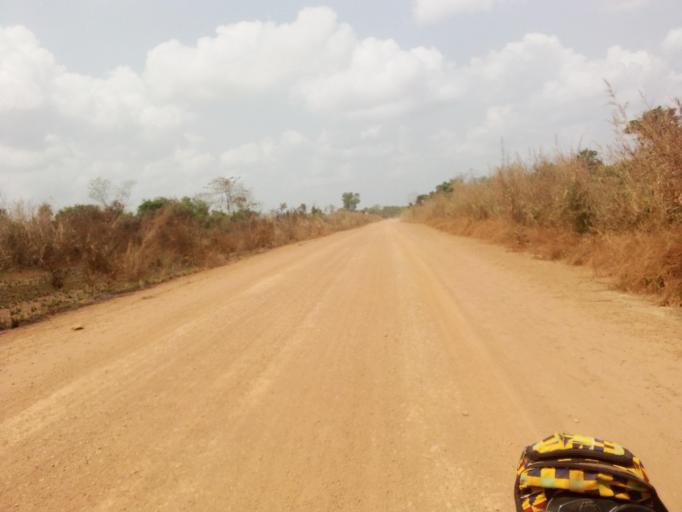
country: SL
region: Southern Province
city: Mogbwemo
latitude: 7.6626
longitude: -12.2703
